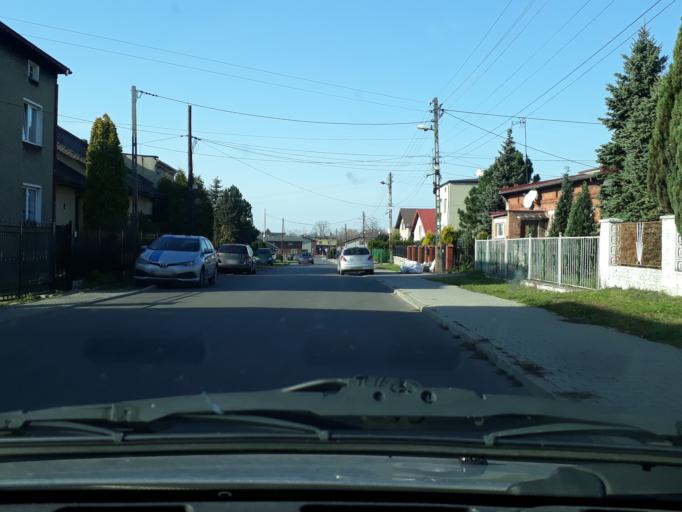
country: PL
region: Silesian Voivodeship
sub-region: Powiat tarnogorski
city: Tarnowskie Gory
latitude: 50.4221
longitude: 18.8800
